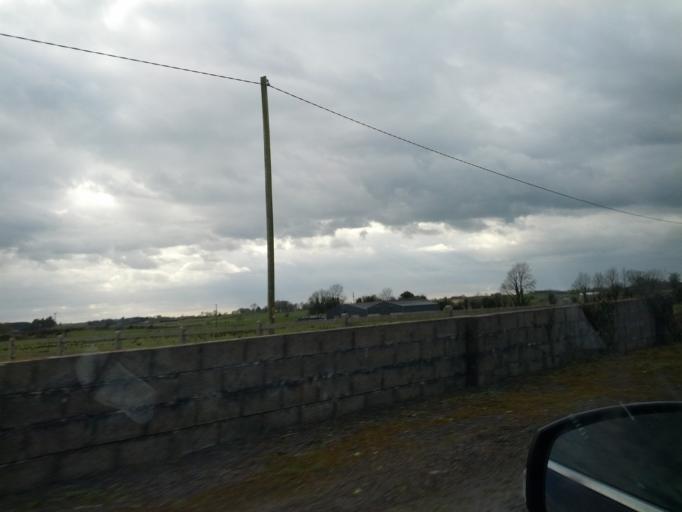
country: IE
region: Connaught
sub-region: County Galway
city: Athenry
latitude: 53.4887
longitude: -8.5882
